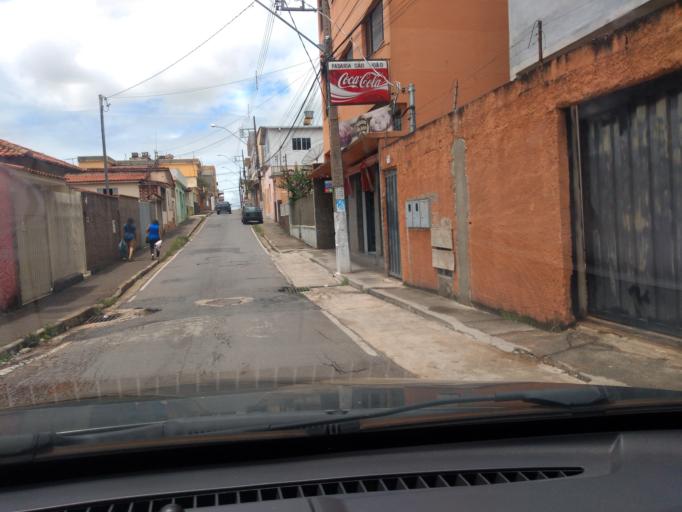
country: BR
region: Minas Gerais
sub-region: Tres Coracoes
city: Tres Coracoes
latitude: -21.6936
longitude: -45.2528
